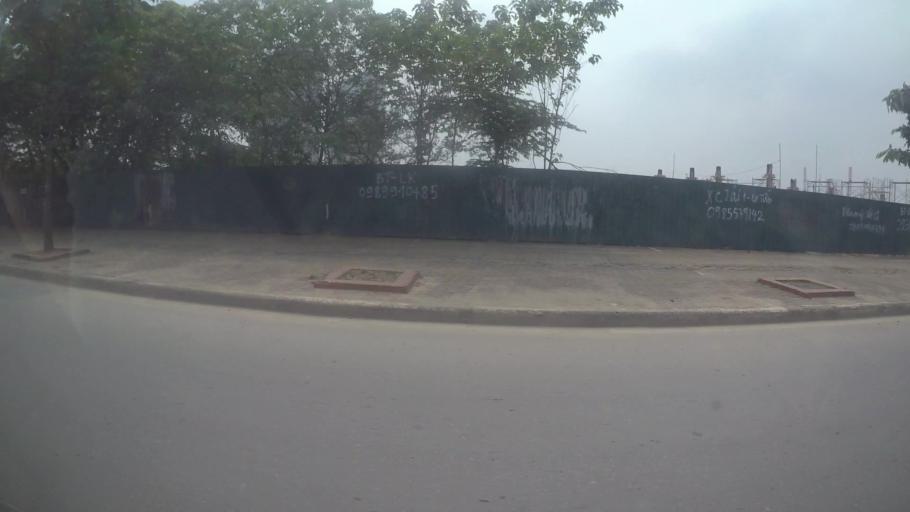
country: VN
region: Ha Noi
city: Thanh Xuan
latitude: 21.0077
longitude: 105.7735
